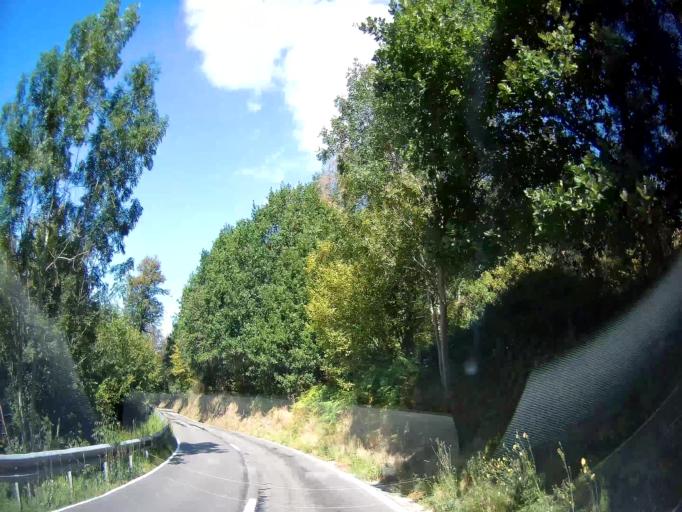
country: BE
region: Wallonia
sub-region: Province du Luxembourg
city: La Roche-en-Ardenne
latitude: 50.1688
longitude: 5.5864
